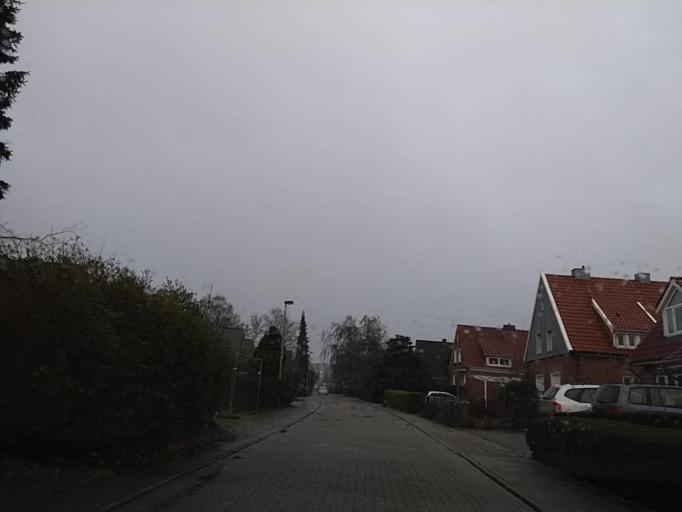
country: DE
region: Lower Saxony
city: Leer
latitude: 53.2347
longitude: 7.4835
